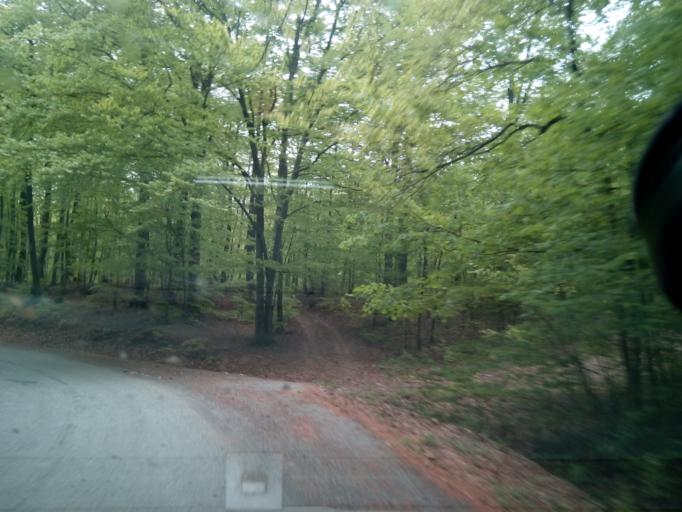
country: SK
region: Kosicky
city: Secovce
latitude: 48.8086
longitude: 21.5148
